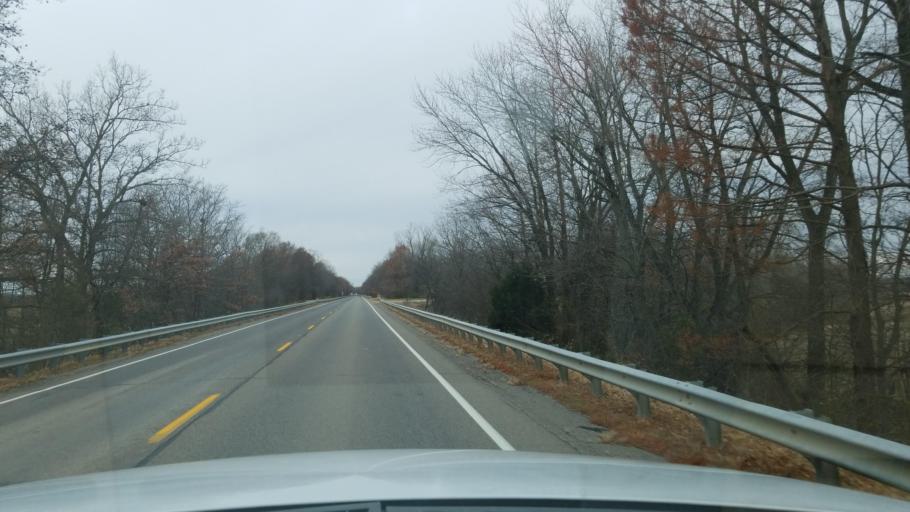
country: US
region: Indiana
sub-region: Posey County
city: Mount Vernon
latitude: 37.9322
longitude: -88.0040
